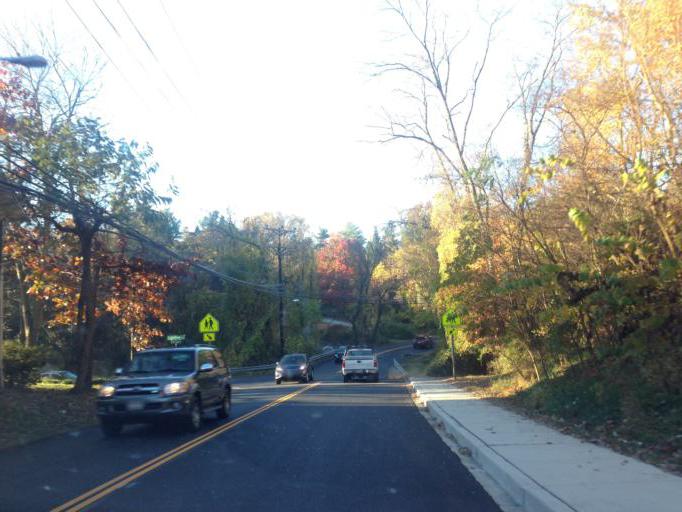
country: US
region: Maryland
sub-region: Baltimore County
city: Pikesville
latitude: 39.3831
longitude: -76.7070
